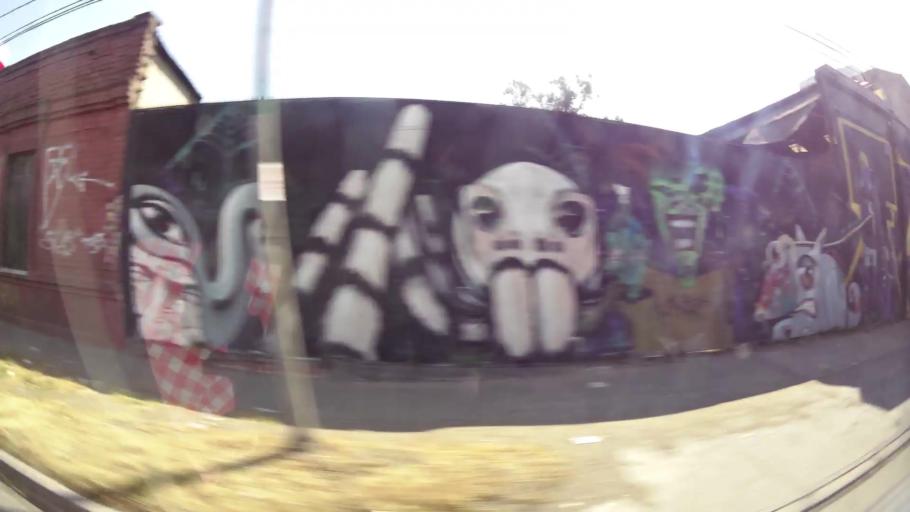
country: CL
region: Santiago Metropolitan
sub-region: Provincia de Santiago
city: Lo Prado
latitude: -33.4417
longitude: -70.6921
